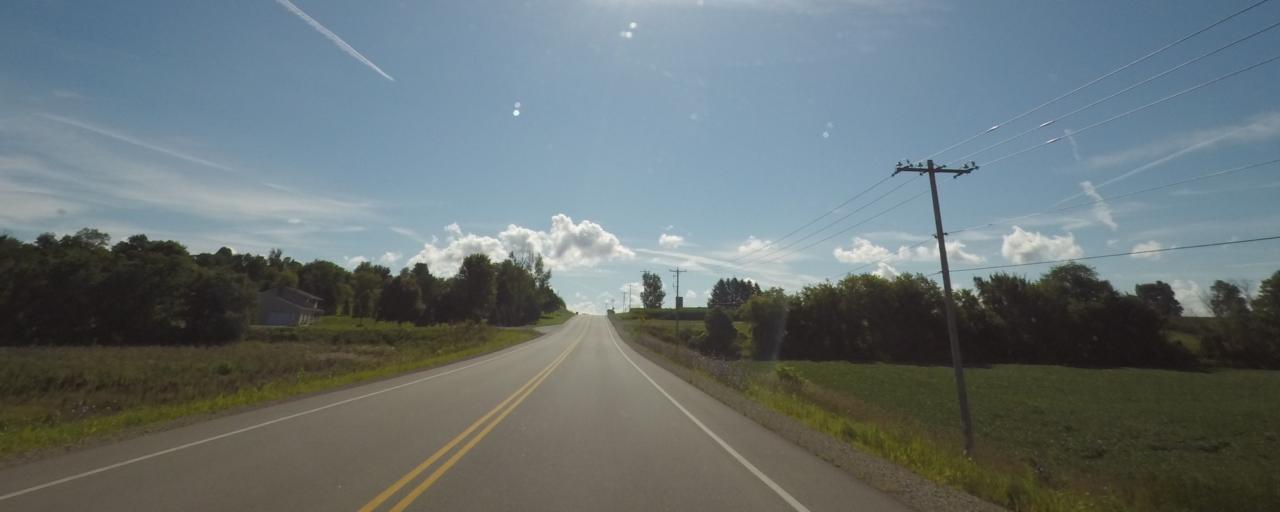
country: US
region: Wisconsin
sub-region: Jefferson County
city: Ixonia
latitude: 43.0729
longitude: -88.6506
